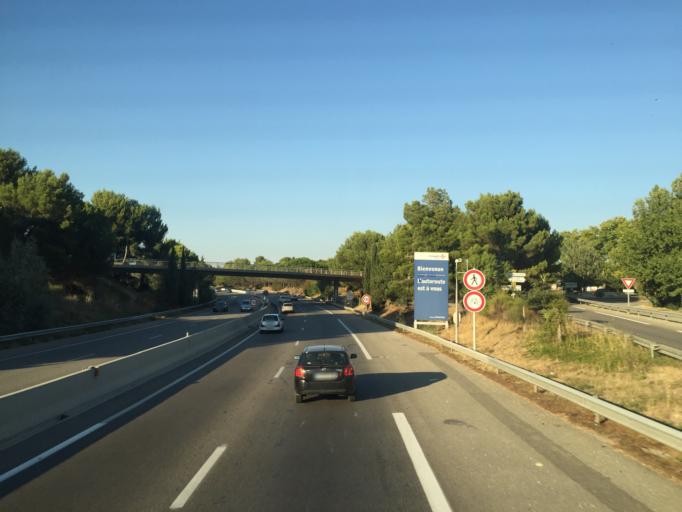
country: FR
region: Provence-Alpes-Cote d'Azur
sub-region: Departement des Bouches-du-Rhone
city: Aix-en-Provence
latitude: 43.5636
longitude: 5.4617
